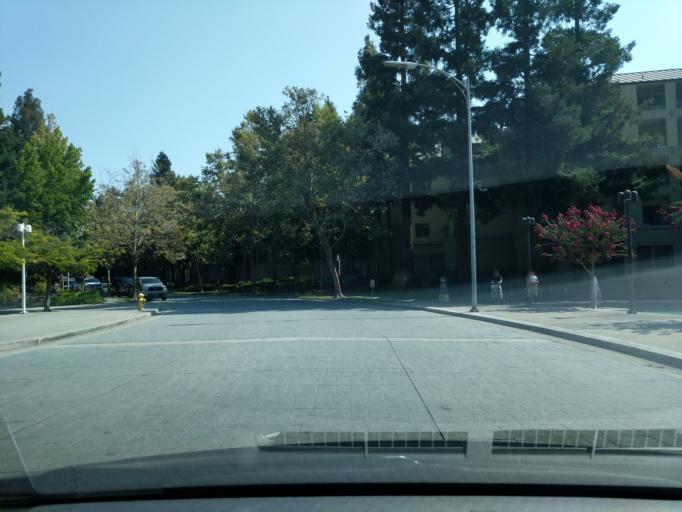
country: US
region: California
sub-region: Santa Clara County
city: Milpitas
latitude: 37.4002
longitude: -121.9242
